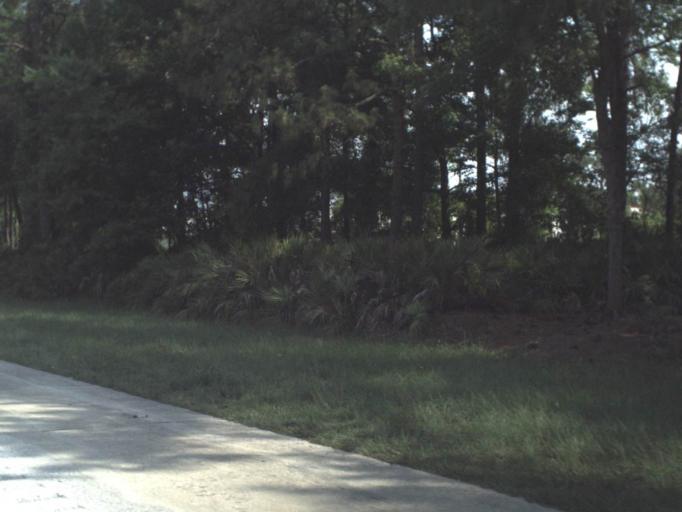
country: US
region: Florida
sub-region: Saint Johns County
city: Fruit Cove
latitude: 30.2113
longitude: -81.5648
